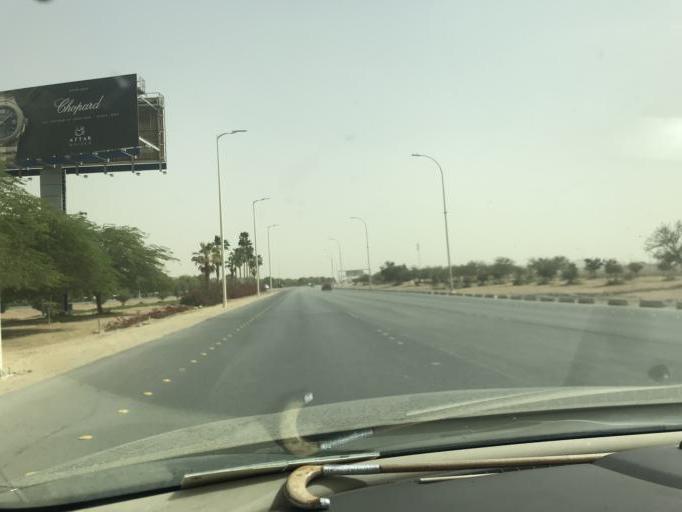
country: SA
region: Ar Riyad
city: Riyadh
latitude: 24.9414
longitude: 46.7072
